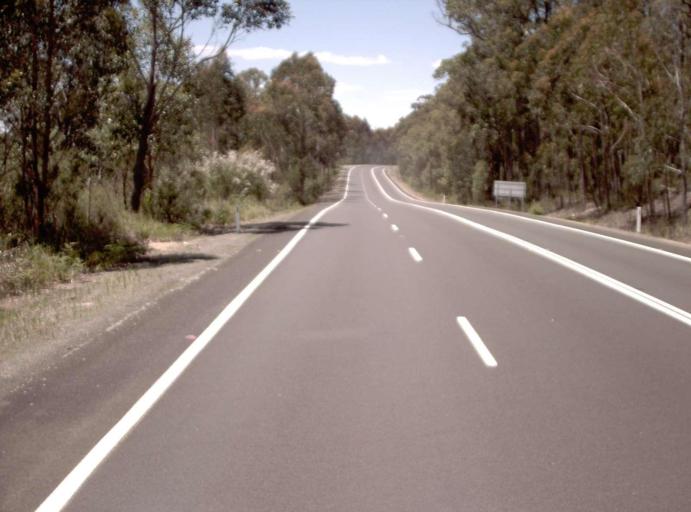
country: AU
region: Victoria
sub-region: East Gippsland
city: Lakes Entrance
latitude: -37.7094
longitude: 148.6836
